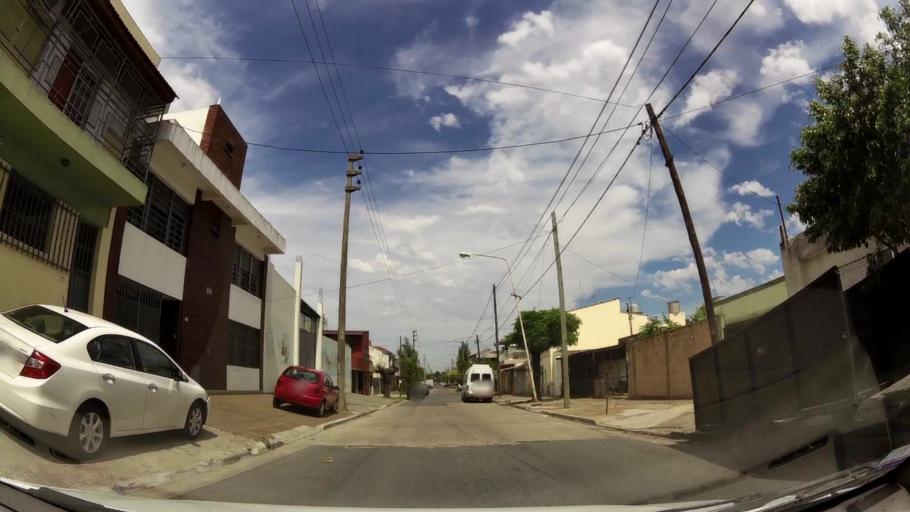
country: AR
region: Buenos Aires
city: San Justo
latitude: -34.6934
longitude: -58.5452
